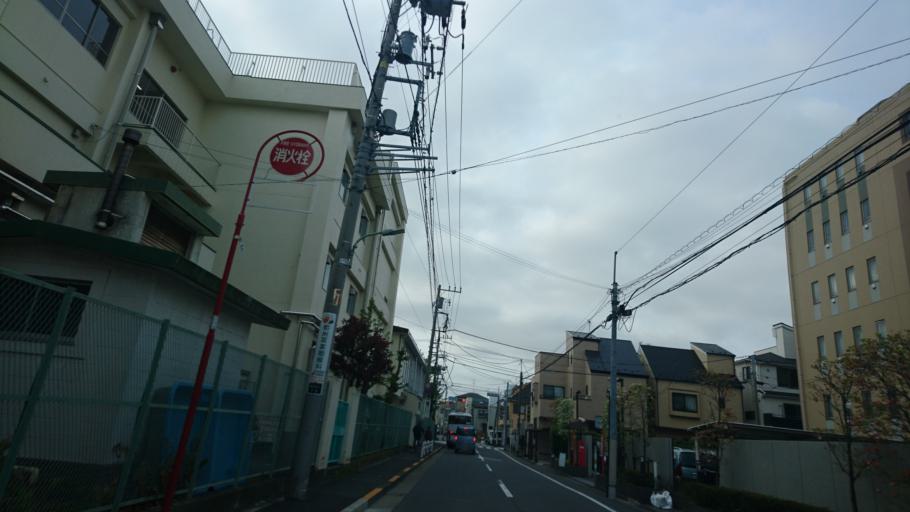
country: JP
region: Kanagawa
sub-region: Kawasaki-shi
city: Kawasaki
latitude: 35.5636
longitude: 139.7047
